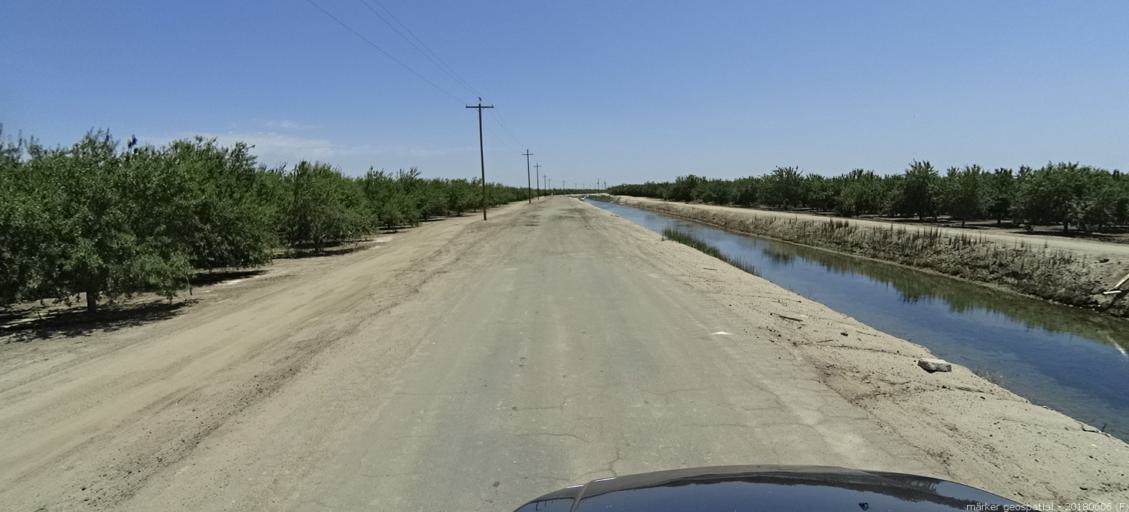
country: US
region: California
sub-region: Fresno County
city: Mendota
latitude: 36.7906
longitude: -120.3190
